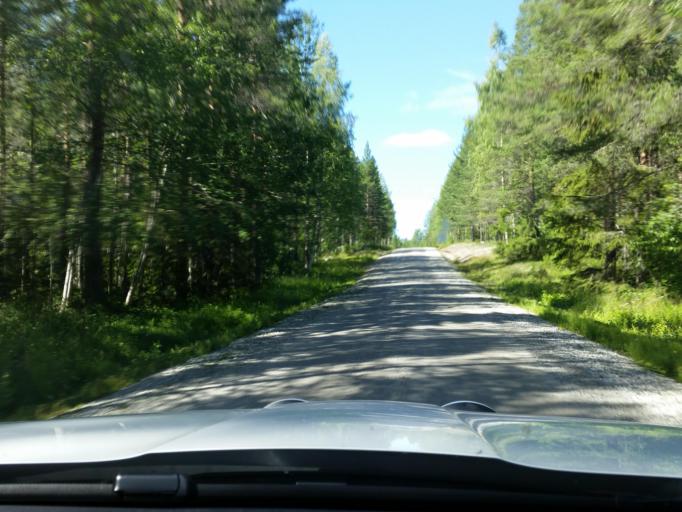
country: SE
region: Vaesterbotten
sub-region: Skelleftea Kommun
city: Storvik
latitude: 65.2189
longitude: 20.8913
